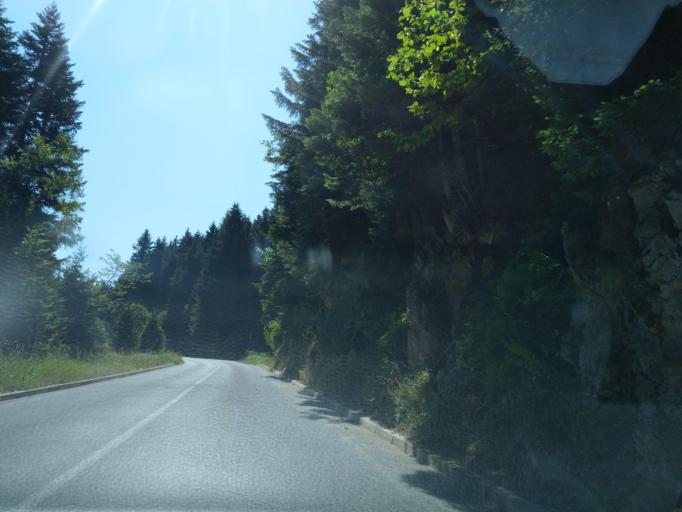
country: RS
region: Central Serbia
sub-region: Zlatiborski Okrug
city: Nova Varos
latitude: 43.4149
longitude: 19.8304
